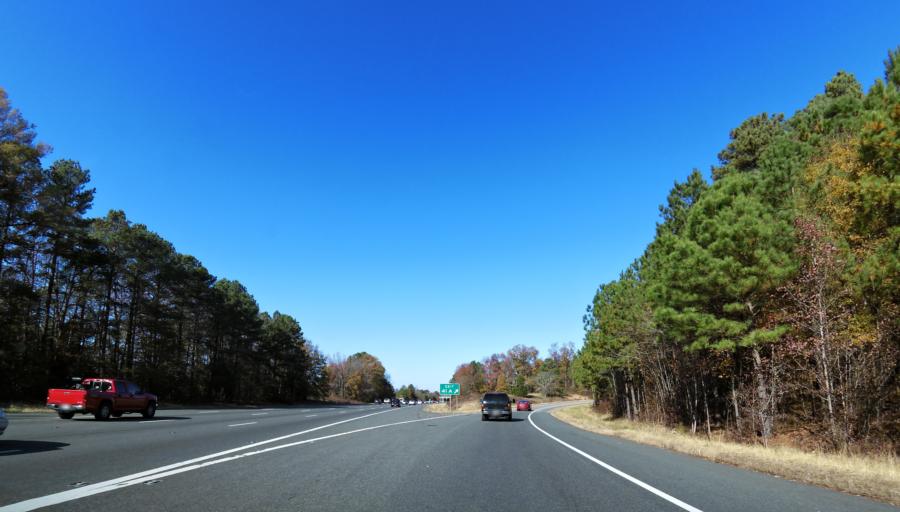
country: US
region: Virginia
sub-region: Henrico County
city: Chamberlayne
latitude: 37.6408
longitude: -77.4084
